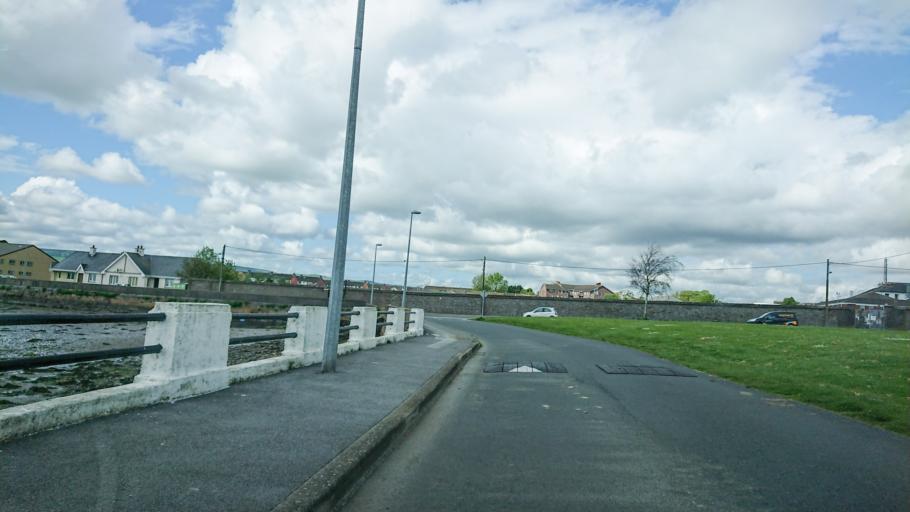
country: IE
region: Munster
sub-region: Waterford
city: Dungarvan
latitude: 52.0863
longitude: -7.6200
